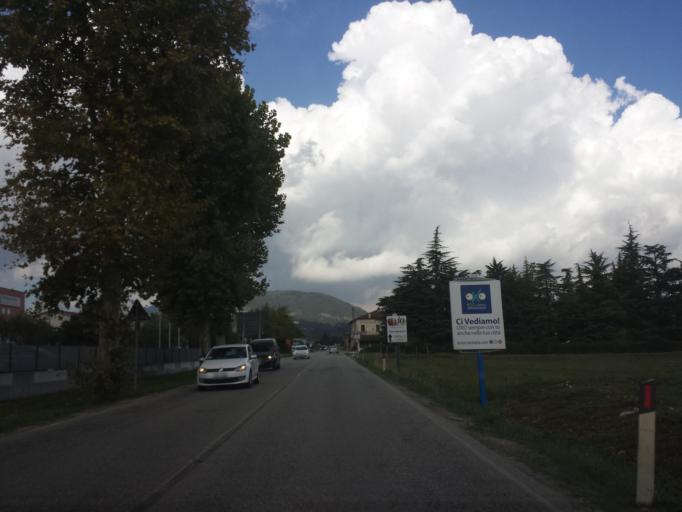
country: IT
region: Veneto
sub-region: Provincia di Vicenza
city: Castelgomberto
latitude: 45.5824
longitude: 11.3814
